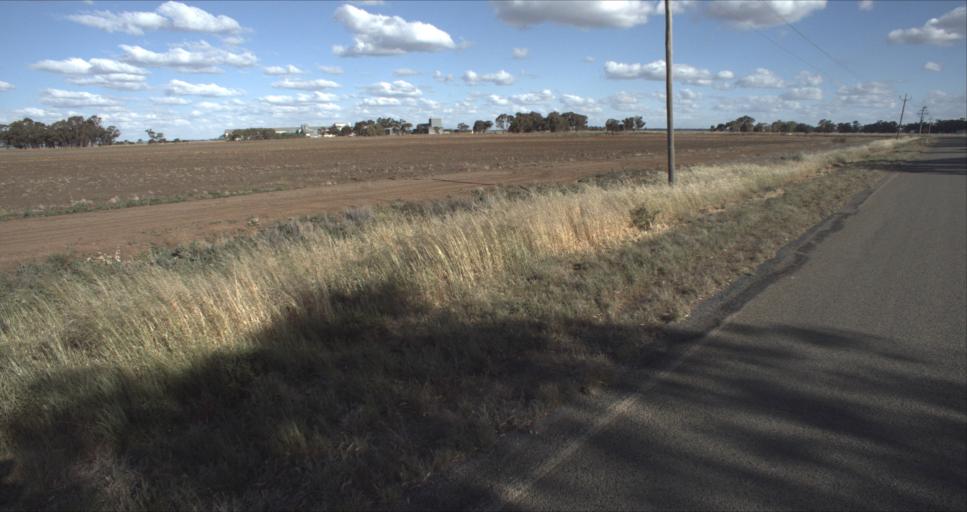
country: AU
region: New South Wales
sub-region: Leeton
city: Leeton
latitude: -34.5511
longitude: 146.2791
